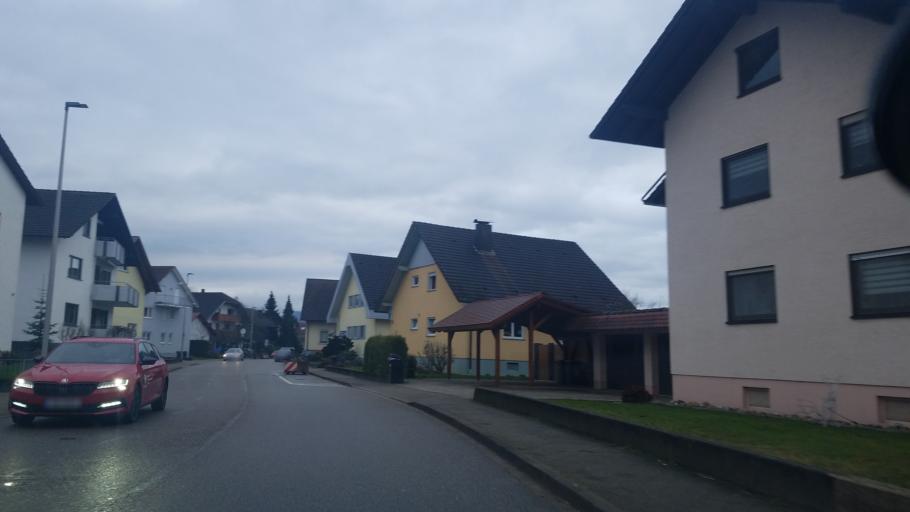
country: DE
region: Baden-Wuerttemberg
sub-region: Karlsruhe Region
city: Ottenhofen
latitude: 48.7212
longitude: 8.1140
